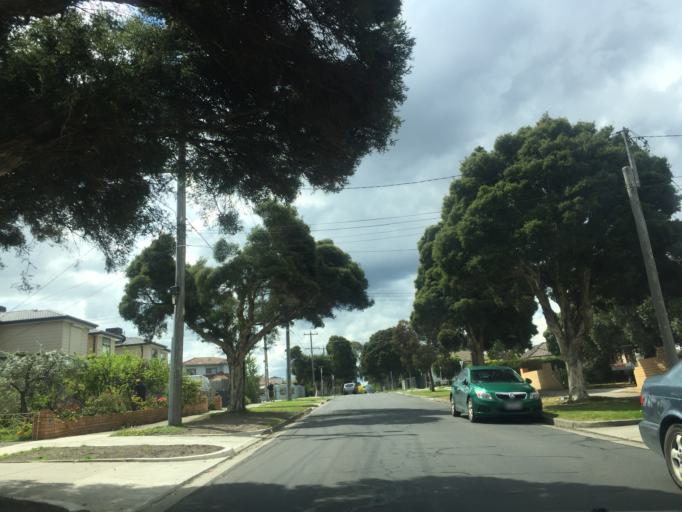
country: AU
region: Victoria
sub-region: Darebin
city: Kingsbury
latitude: -37.7077
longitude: 145.0199
